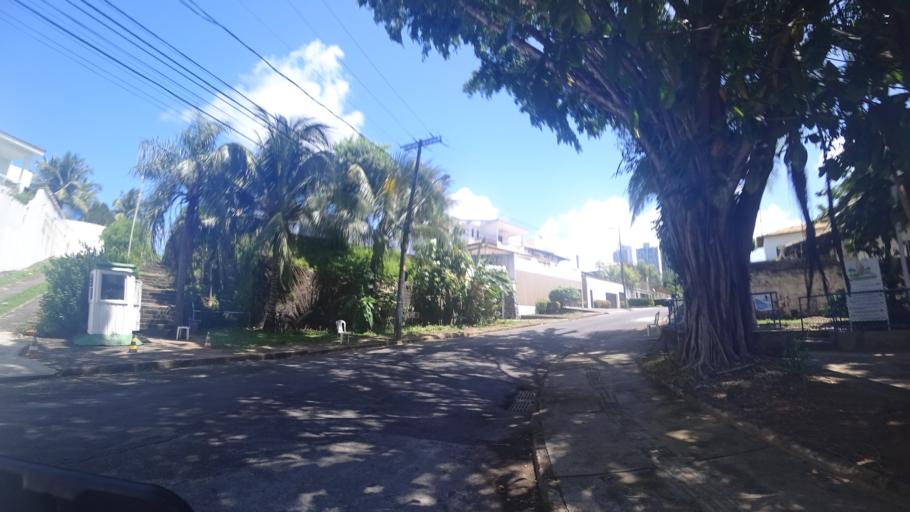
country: BR
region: Bahia
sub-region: Salvador
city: Salvador
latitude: -12.9925
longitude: -38.4689
